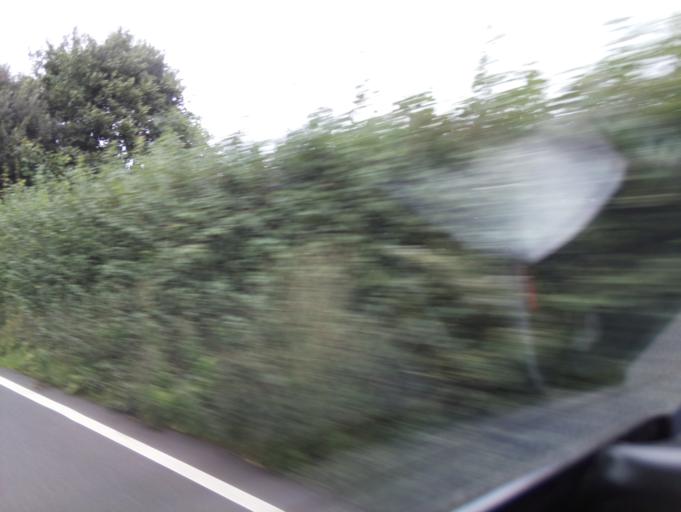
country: GB
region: England
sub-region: Devon
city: Exminster
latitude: 50.6718
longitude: -3.4844
